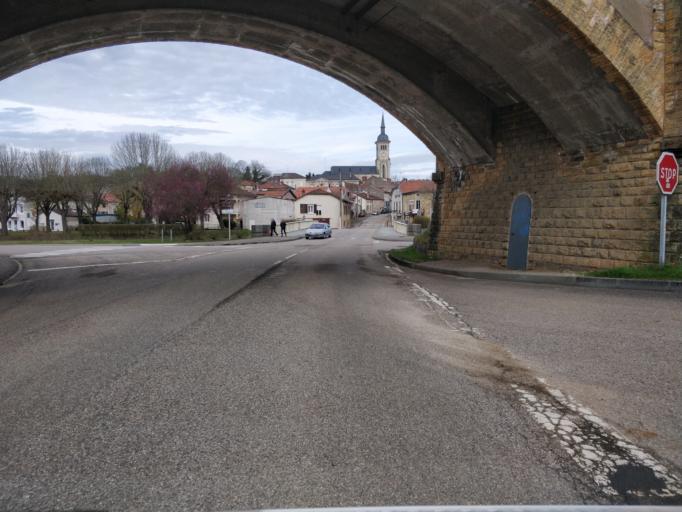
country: FR
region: Lorraine
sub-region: Departement de Meurthe-et-Moselle
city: Pagny-sur-Moselle
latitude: 48.9519
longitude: 5.8681
